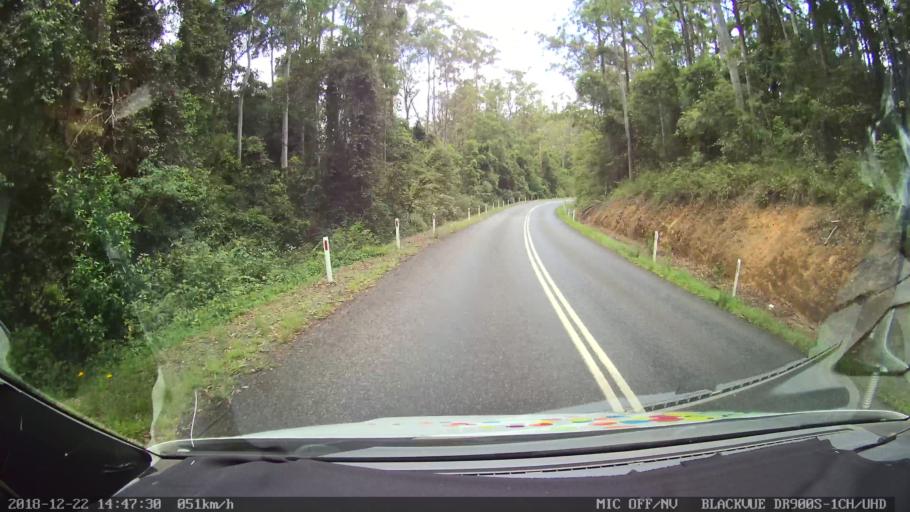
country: AU
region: New South Wales
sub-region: Bellingen
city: Dorrigo
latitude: -30.1762
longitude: 152.5562
